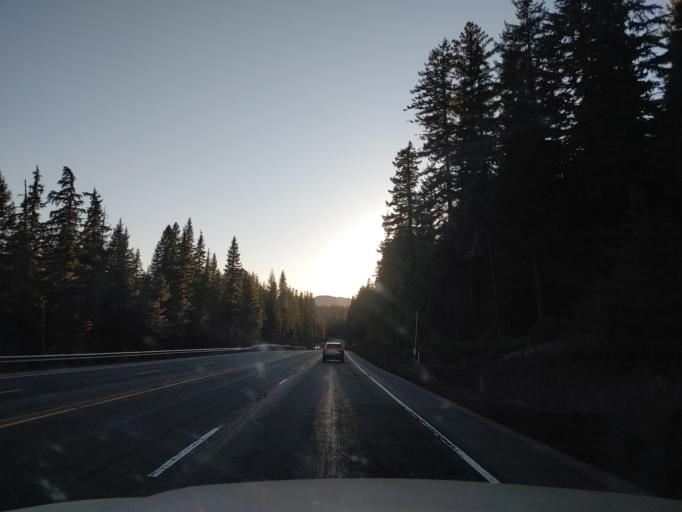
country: US
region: Oregon
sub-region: Lane County
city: Oakridge
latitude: 43.6169
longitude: -122.0885
